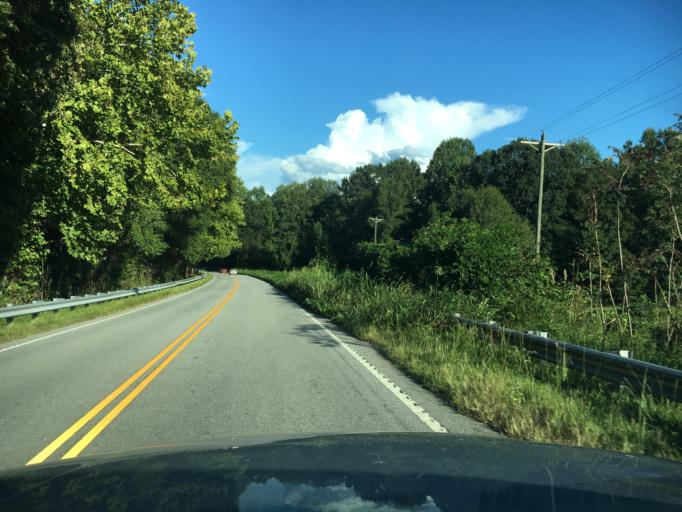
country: US
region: South Carolina
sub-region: Greenville County
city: Five Forks
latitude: 34.7933
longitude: -82.1373
